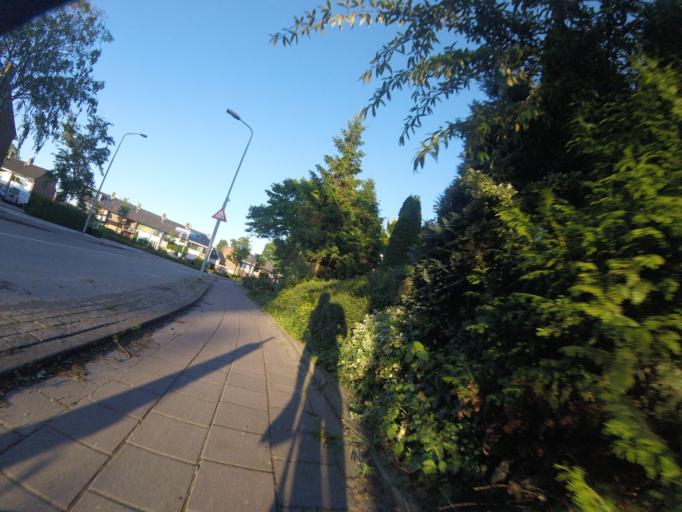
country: NL
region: North Holland
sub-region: Gemeente Haarlemmermeer
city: Hoofddorp
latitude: 52.3736
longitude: 4.7459
